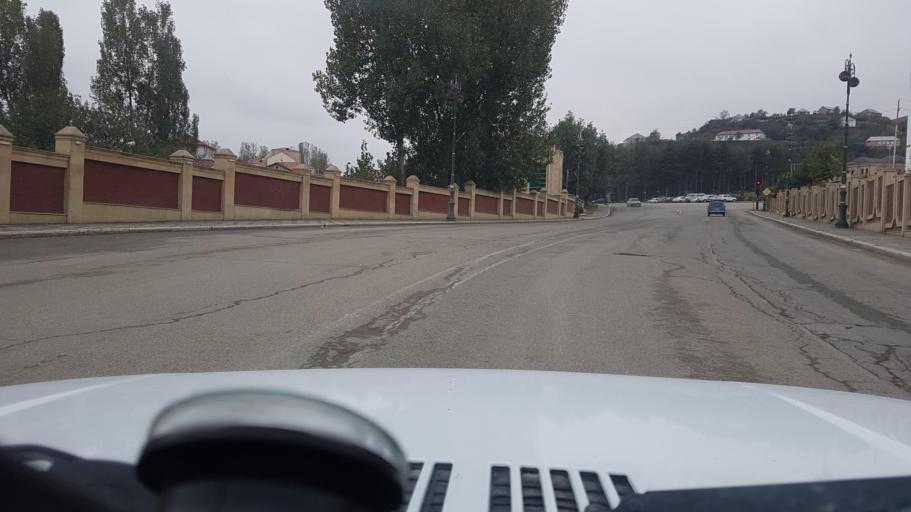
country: AZ
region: Gadabay Rayon
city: Kyadabek
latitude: 40.5806
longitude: 45.8100
